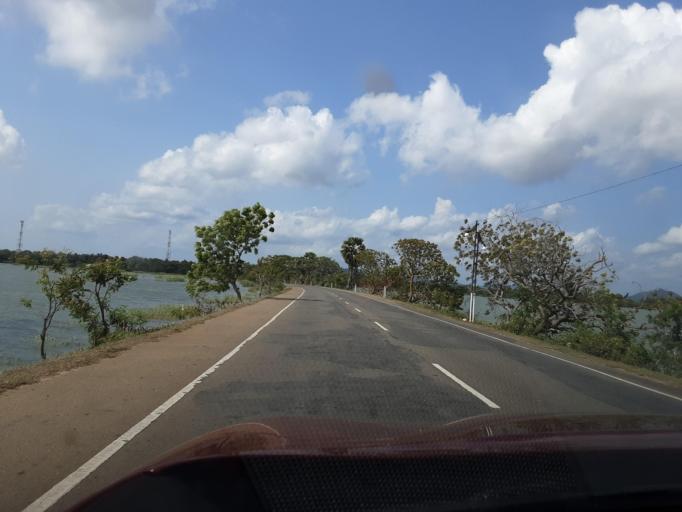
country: LK
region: Southern
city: Tangalla
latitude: 6.2889
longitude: 81.2340
